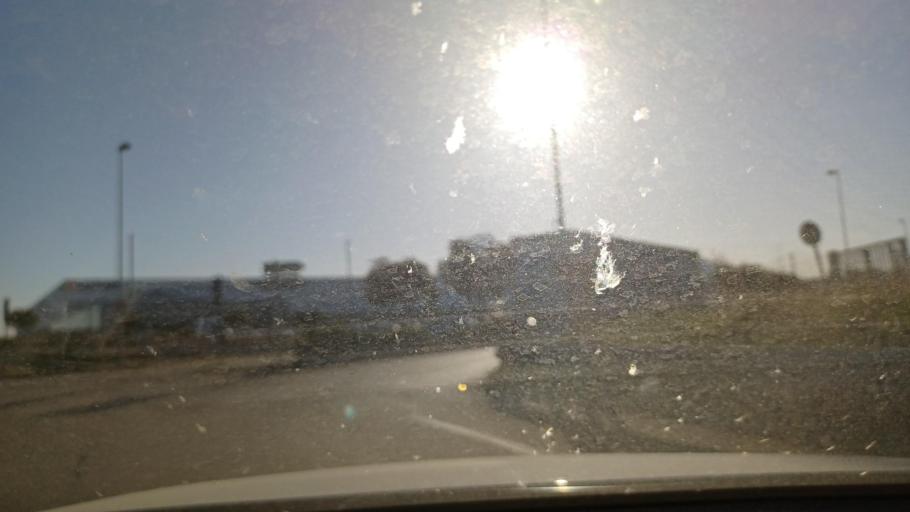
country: ES
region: Catalonia
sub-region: Provincia de Barcelona
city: Ripollet
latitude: 41.5188
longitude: 2.1534
